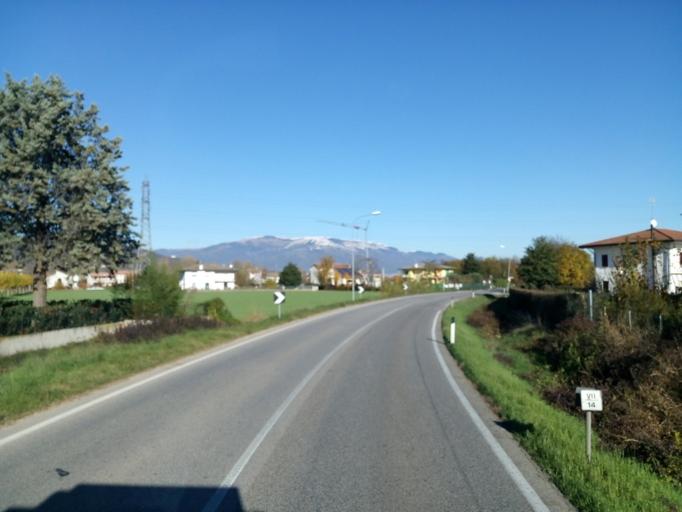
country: IT
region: Veneto
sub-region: Provincia di Treviso
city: Caerano di San Marco
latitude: 45.7952
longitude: 11.9946
